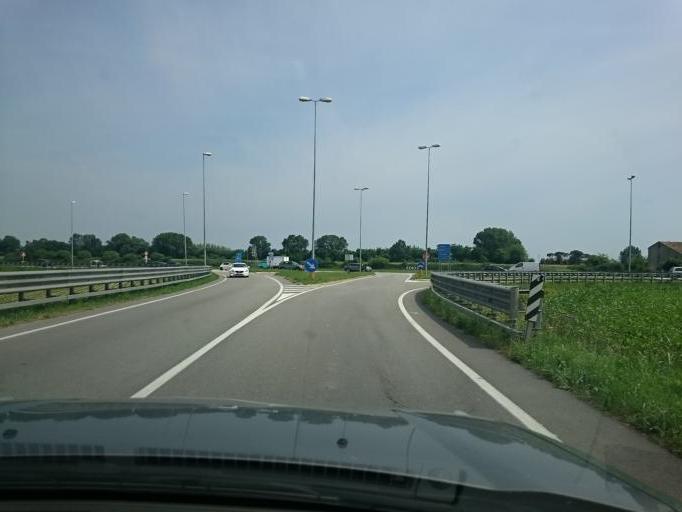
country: IT
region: Veneto
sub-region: Provincia di Padova
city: Codevigo
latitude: 45.2533
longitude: 12.1307
